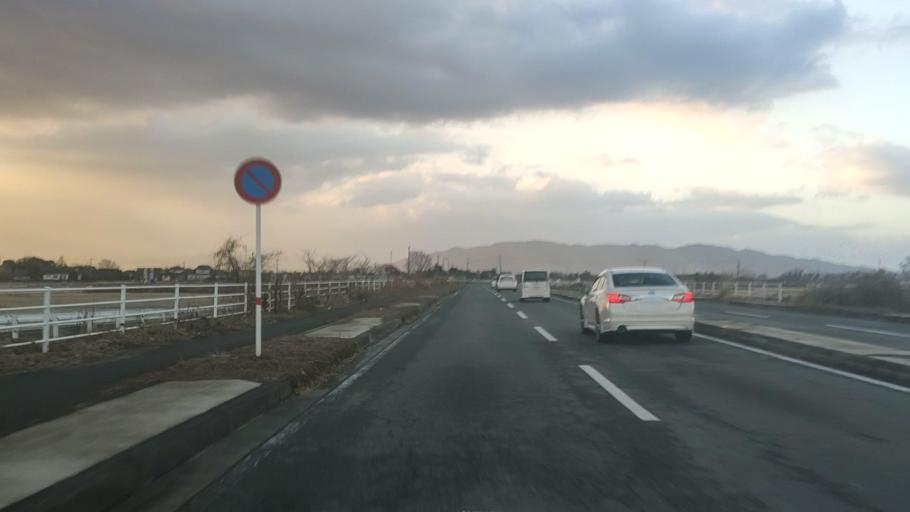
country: JP
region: Kumamoto
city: Kumamoto
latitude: 32.7503
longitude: 130.7069
